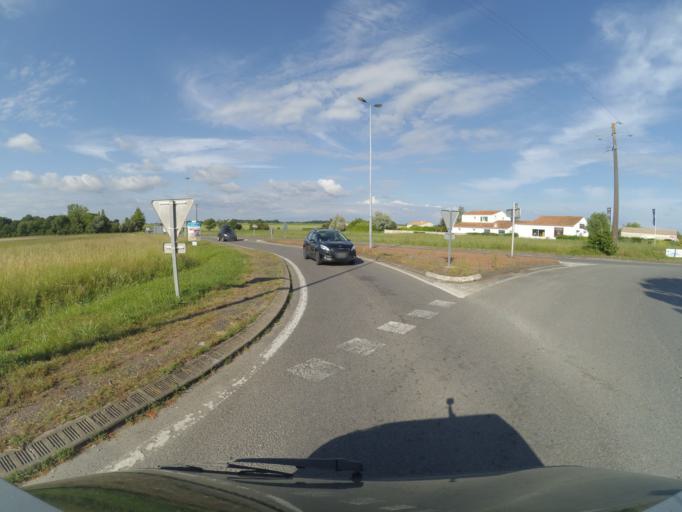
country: FR
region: Poitou-Charentes
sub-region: Departement de la Charente-Maritime
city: Le Gua
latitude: 45.7325
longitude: -0.9559
